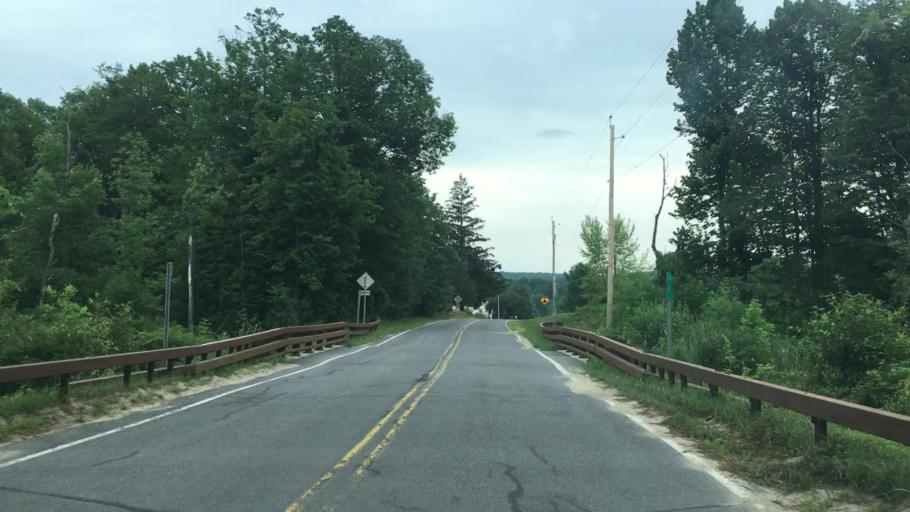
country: US
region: New York
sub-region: Clinton County
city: Peru
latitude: 44.5255
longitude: -73.5744
